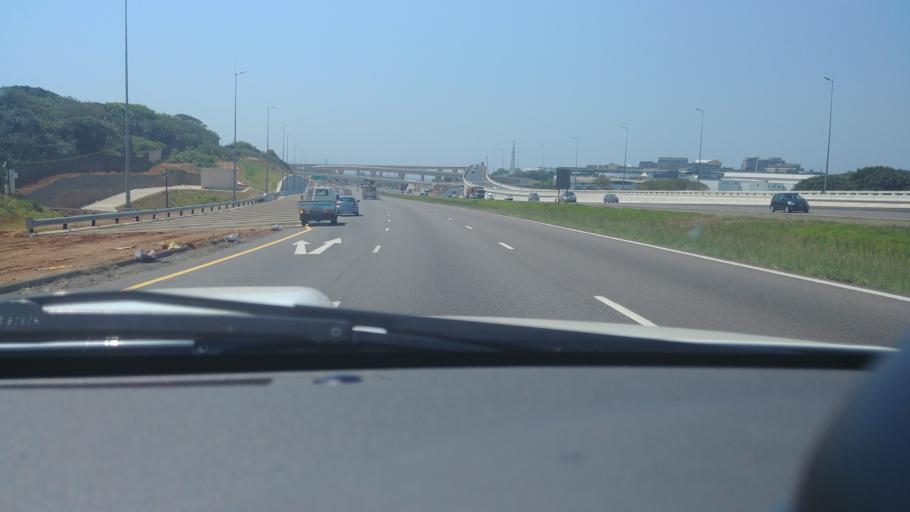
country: ZA
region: KwaZulu-Natal
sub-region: eThekwini Metropolitan Municipality
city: Durban
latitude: -29.7308
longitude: 31.0560
